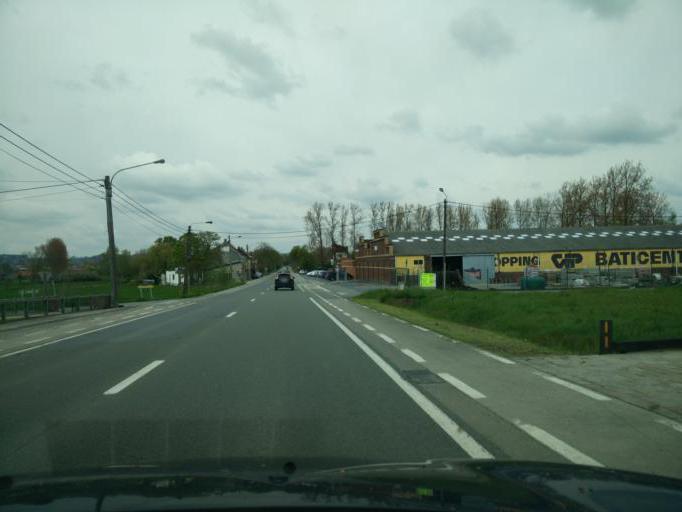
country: BE
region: Flanders
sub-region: Provincie Oost-Vlaanderen
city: Ronse
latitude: 50.7205
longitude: 3.5828
